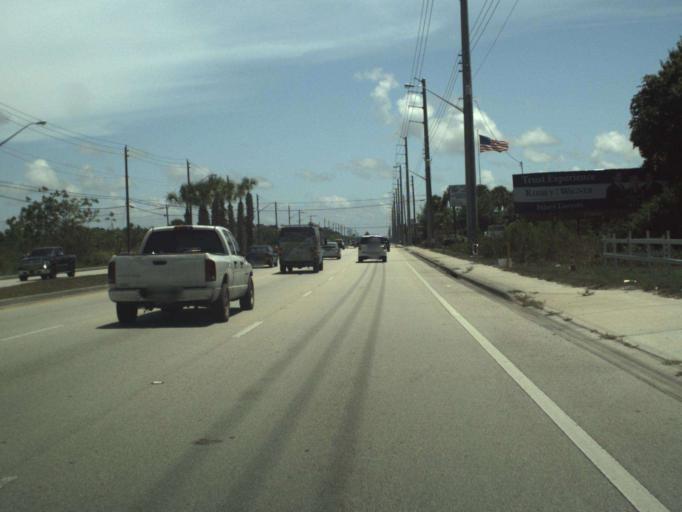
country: US
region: Florida
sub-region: Saint Lucie County
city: White City
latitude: 27.3612
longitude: -80.3260
